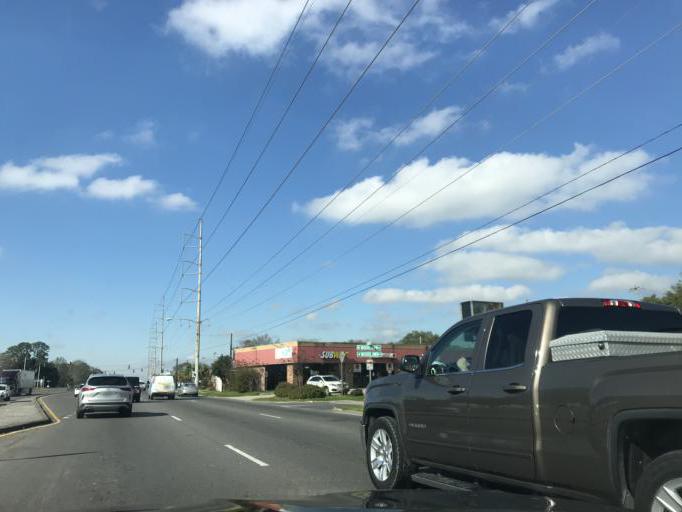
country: US
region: Louisiana
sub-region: Jefferson Parish
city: Metairie Terrace
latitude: 29.9754
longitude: -90.1758
